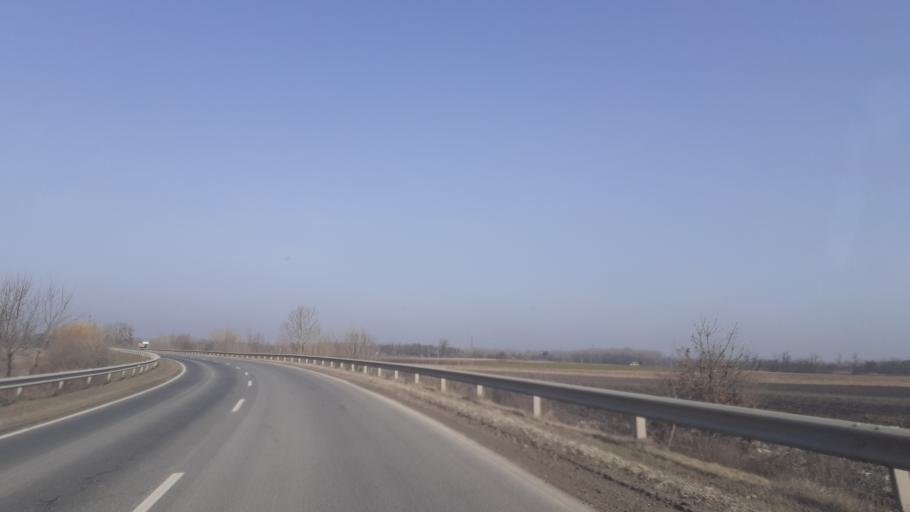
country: HU
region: Pest
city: Bugyi
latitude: 47.2365
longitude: 19.1206
